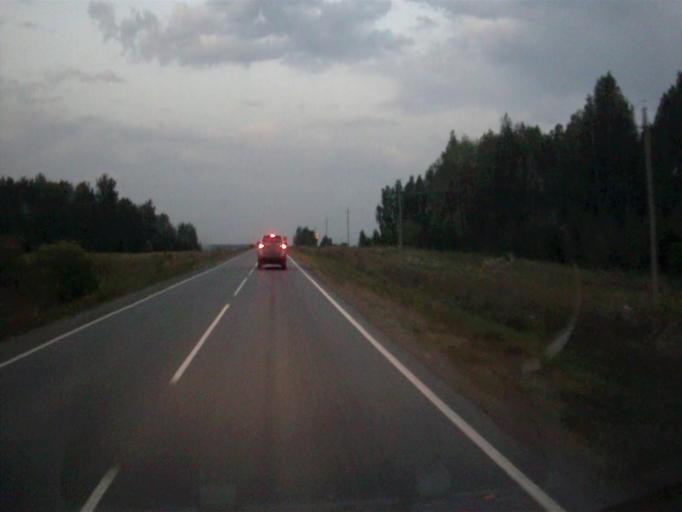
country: RU
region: Chelyabinsk
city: Timiryazevskiy
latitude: 55.2057
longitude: 60.7876
